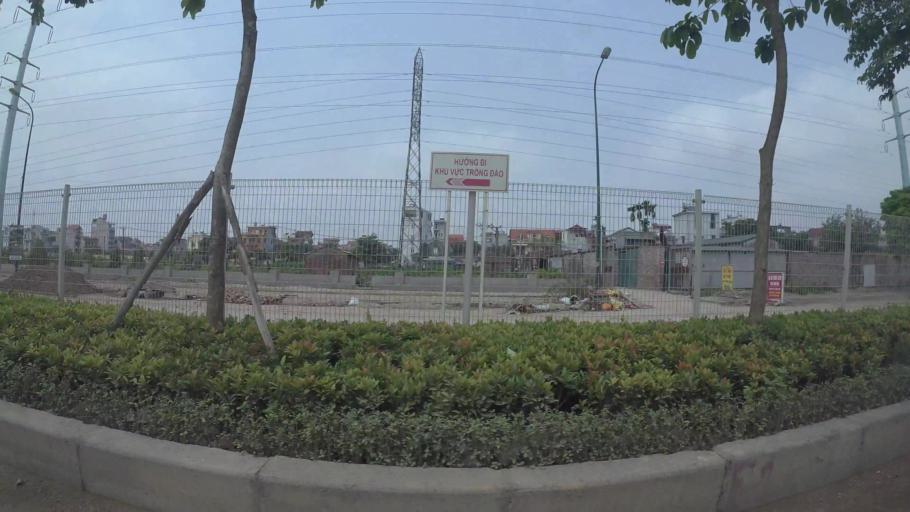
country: VN
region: Ha Noi
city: Tay Ho
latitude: 21.0852
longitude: 105.8020
